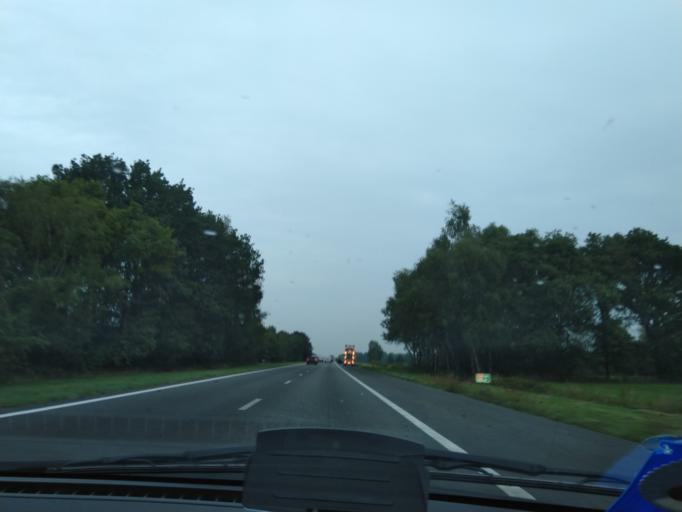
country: NL
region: Drenthe
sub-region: Gemeente Hoogeveen
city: Hoogeveen
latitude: 52.7544
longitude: 6.4560
